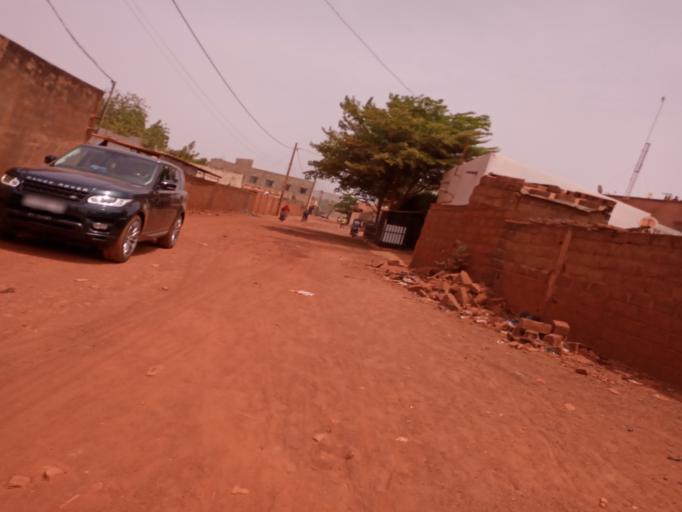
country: ML
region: Bamako
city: Bamako
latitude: 12.6725
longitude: -7.9107
